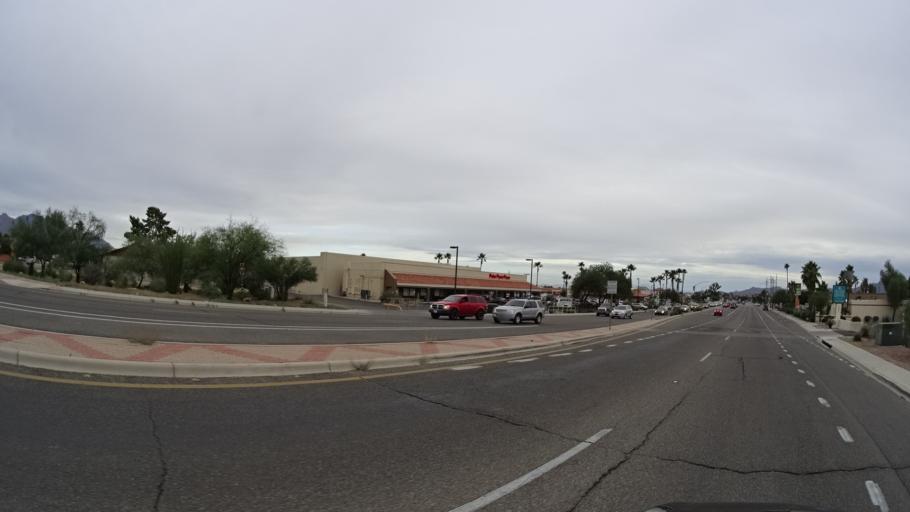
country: US
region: Arizona
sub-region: Pima County
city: Casas Adobes
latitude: 32.3398
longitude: -111.0470
